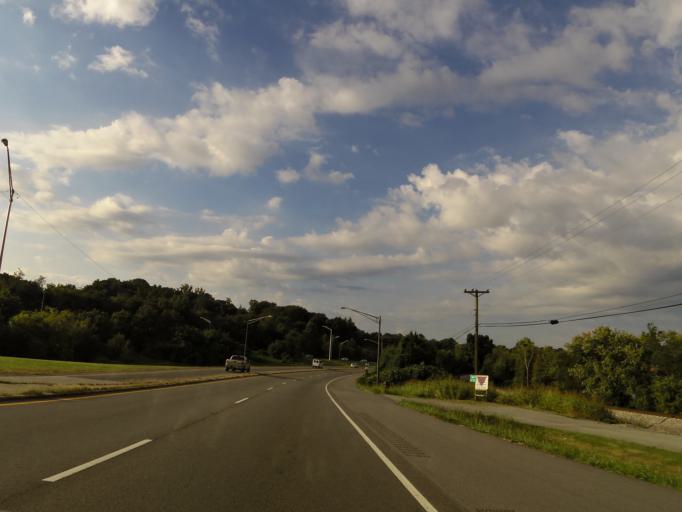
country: US
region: Tennessee
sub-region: Knox County
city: Knoxville
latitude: 35.8853
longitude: -83.9551
